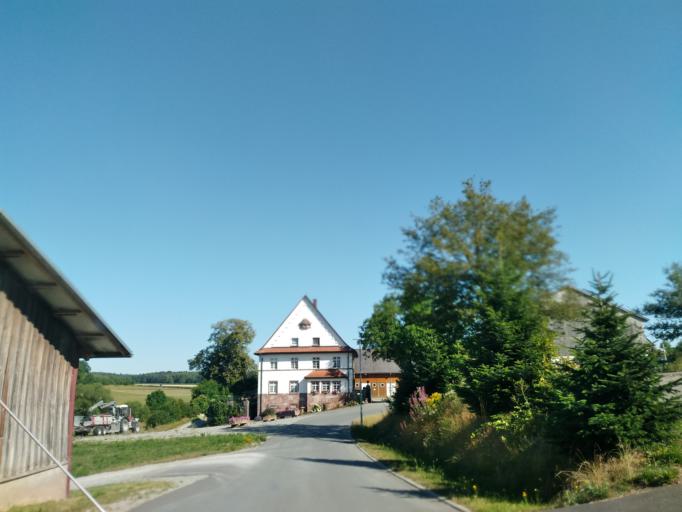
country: DE
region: Baden-Wuerttemberg
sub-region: Karlsruhe Region
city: Mudau
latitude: 49.5355
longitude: 9.2426
